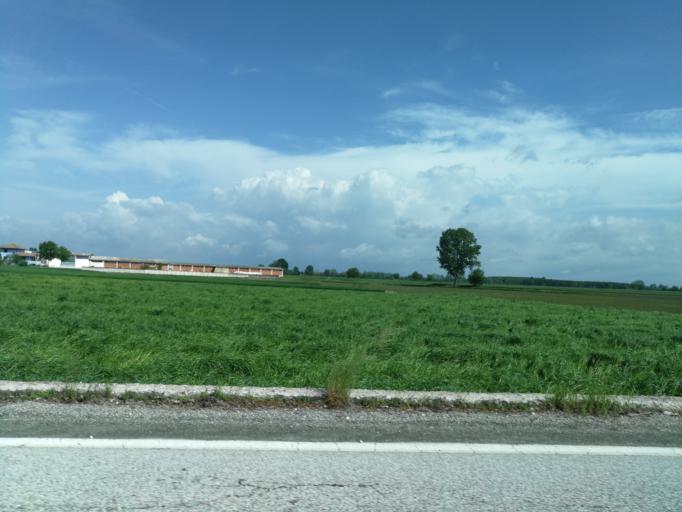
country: IT
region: Piedmont
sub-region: Provincia di Cuneo
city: Faule
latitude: 44.7994
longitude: 7.5765
